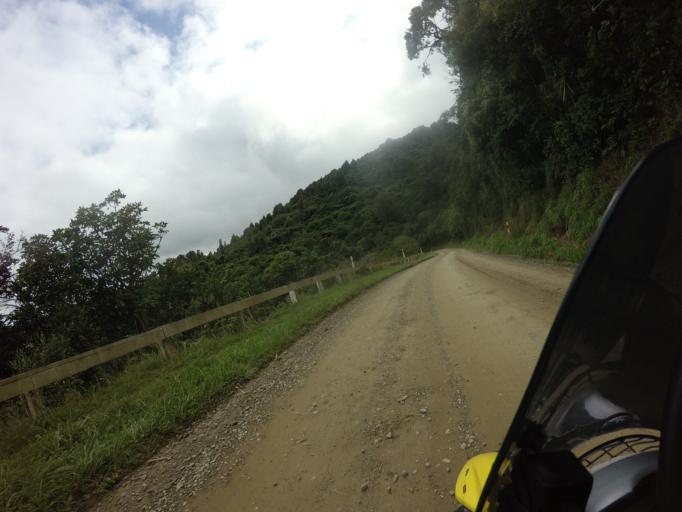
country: NZ
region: Hawke's Bay
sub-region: Wairoa District
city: Wairoa
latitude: -38.7810
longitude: 177.1306
